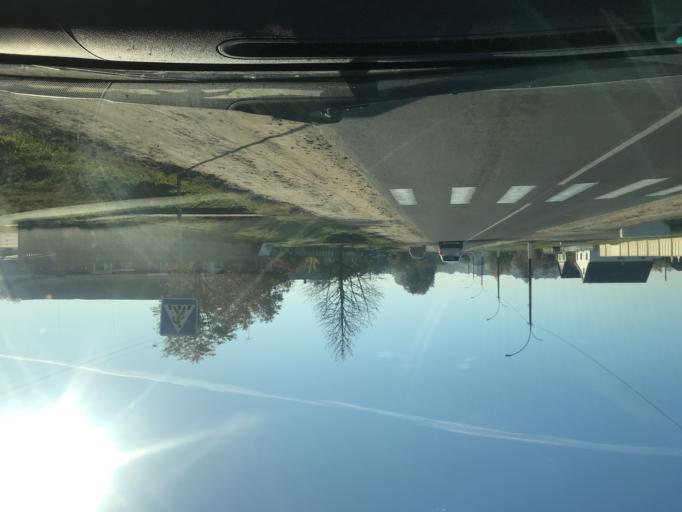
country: BY
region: Brest
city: Ivanava
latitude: 52.1432
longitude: 25.5189
